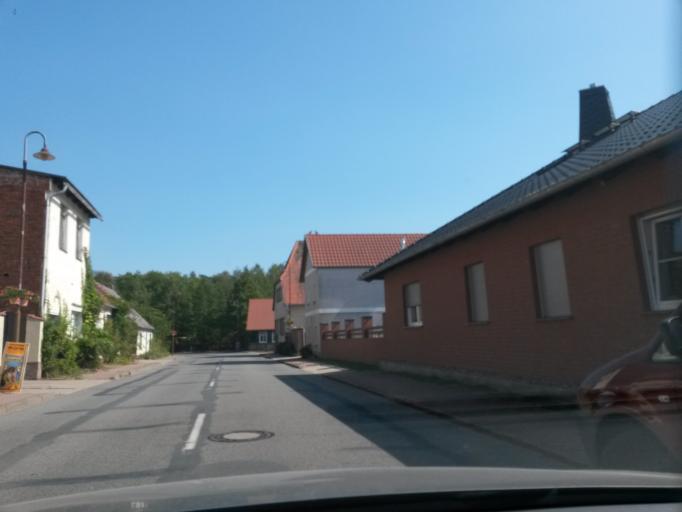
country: DE
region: Saxony-Anhalt
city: Jerichow
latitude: 52.4700
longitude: 12.0216
